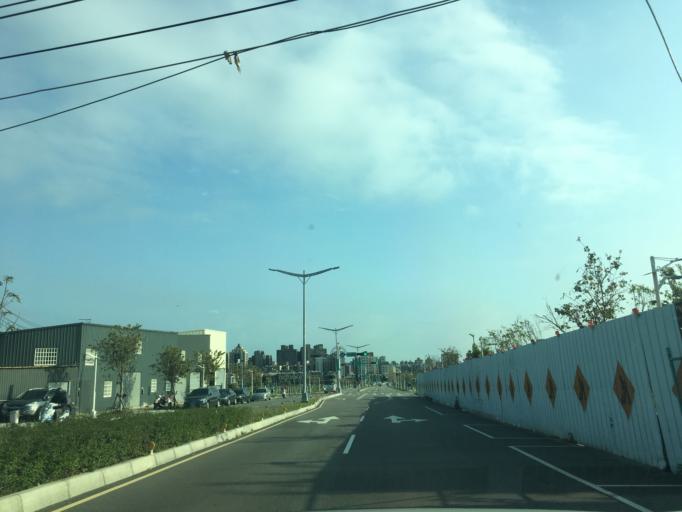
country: TW
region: Taiwan
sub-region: Taichung City
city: Taichung
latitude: 24.1915
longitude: 120.6934
